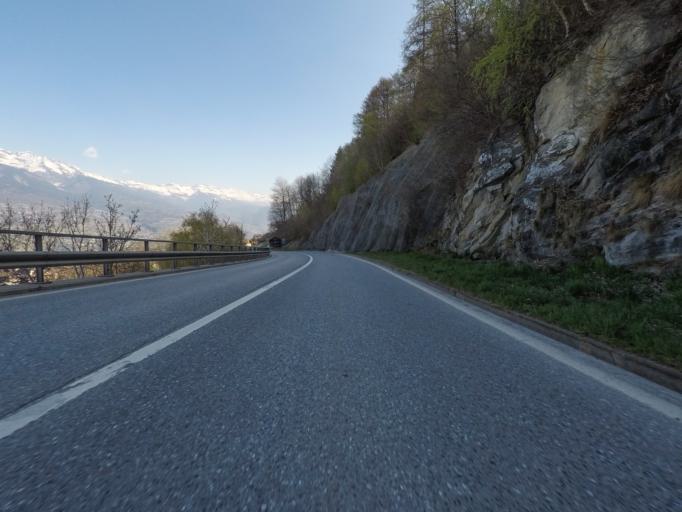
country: CH
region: Valais
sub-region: Conthey District
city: Basse-Nendaz
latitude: 46.2021
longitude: 7.3276
